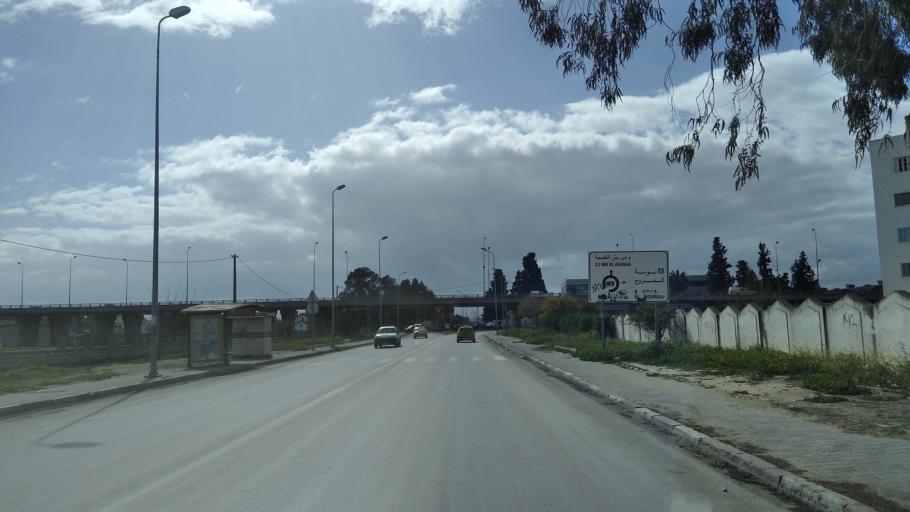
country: TN
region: Bin 'Arus
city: Ben Arous
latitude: 36.7427
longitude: 10.2266
